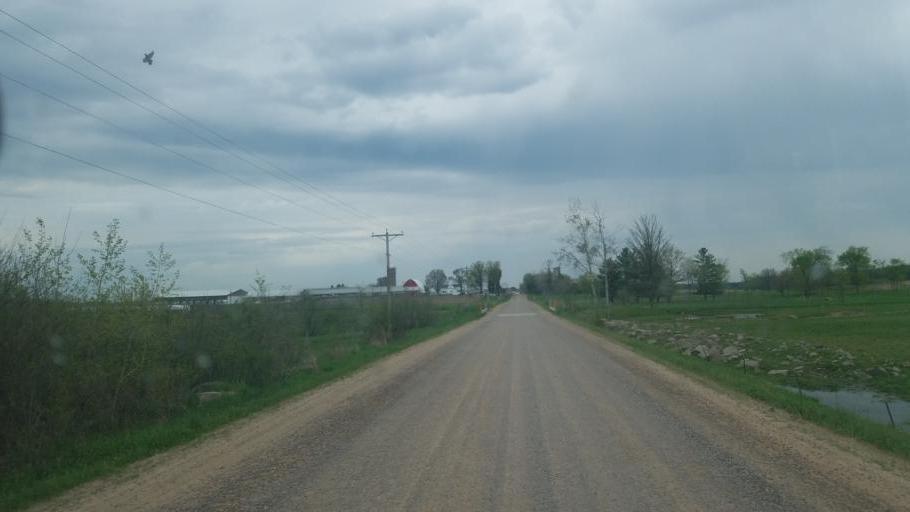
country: US
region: Wisconsin
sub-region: Clark County
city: Loyal
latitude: 44.6376
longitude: -90.4565
